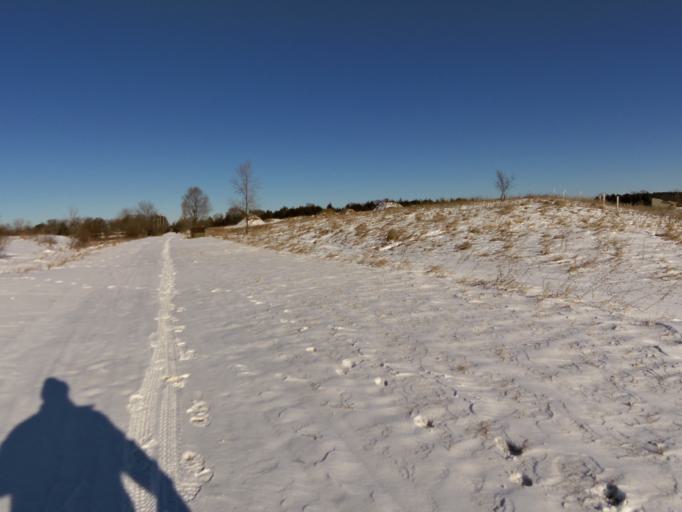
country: US
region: Minnesota
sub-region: Washington County
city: Lake Elmo
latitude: 44.9928
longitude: -92.8984
